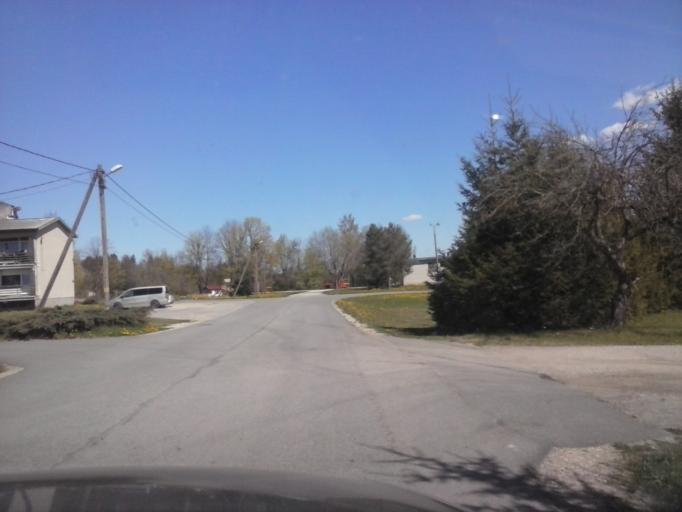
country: EE
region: Valgamaa
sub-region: Torva linn
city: Torva
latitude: 58.1501
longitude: 25.9767
